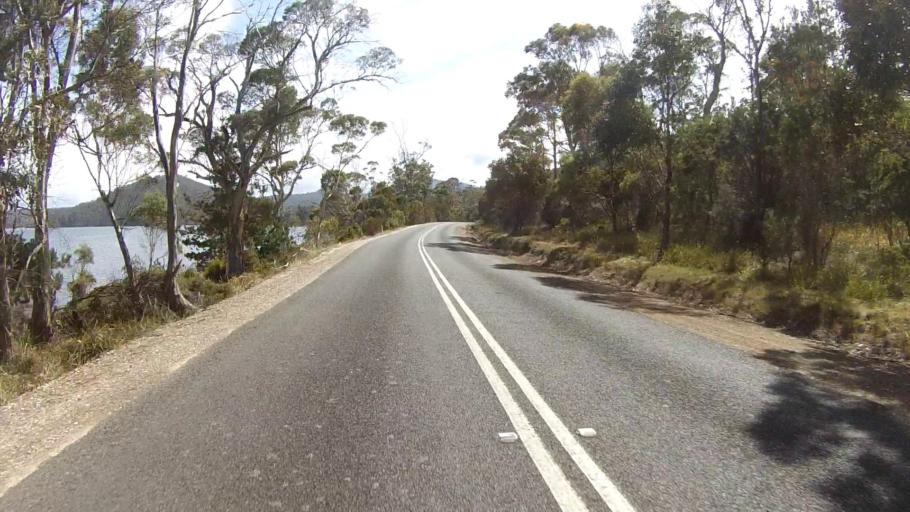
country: AU
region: Tasmania
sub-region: Huon Valley
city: Cygnet
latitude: -43.2643
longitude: 147.1429
